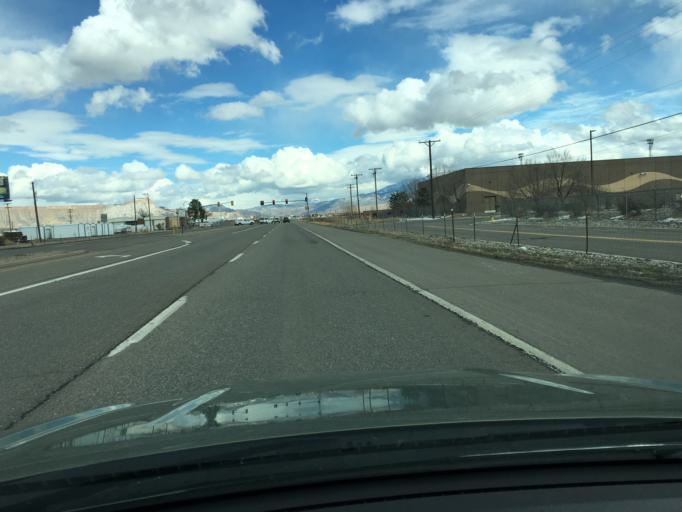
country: US
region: Colorado
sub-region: Mesa County
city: Grand Junction
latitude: 39.0685
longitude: -108.5356
